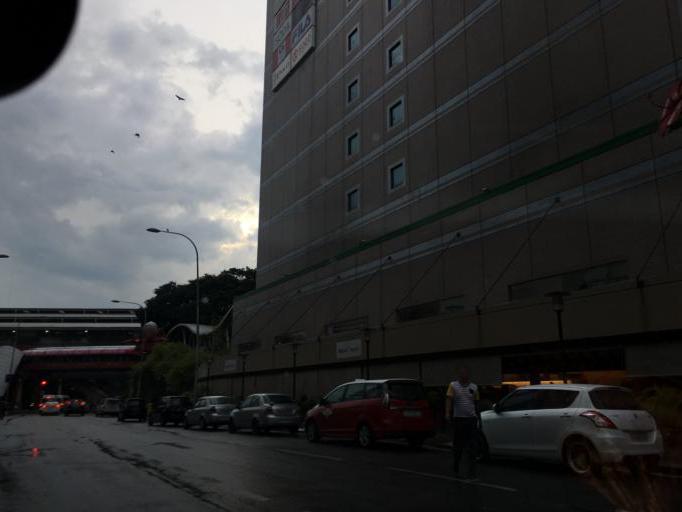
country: MY
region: Kuala Lumpur
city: Kuala Lumpur
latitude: 3.1558
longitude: 101.6957
